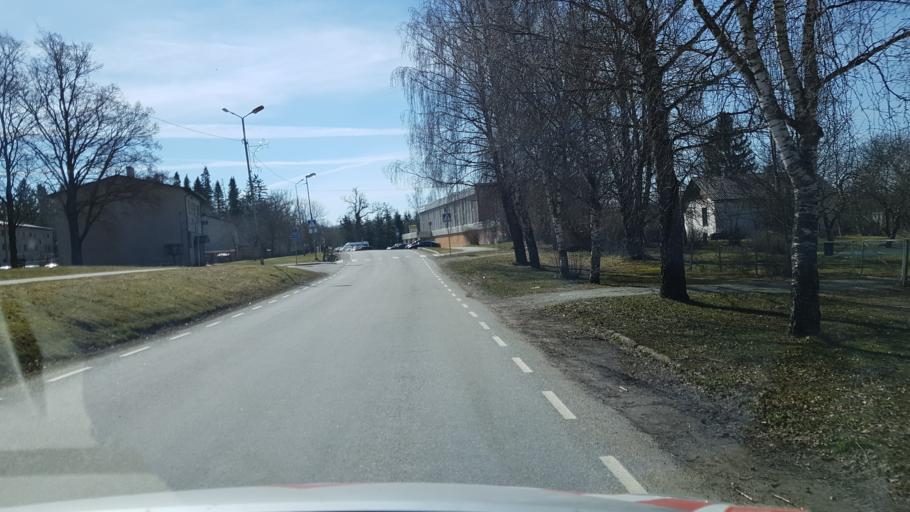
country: EE
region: Laeaene-Virumaa
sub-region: Vinni vald
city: Vinni
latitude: 59.2913
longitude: 26.4273
